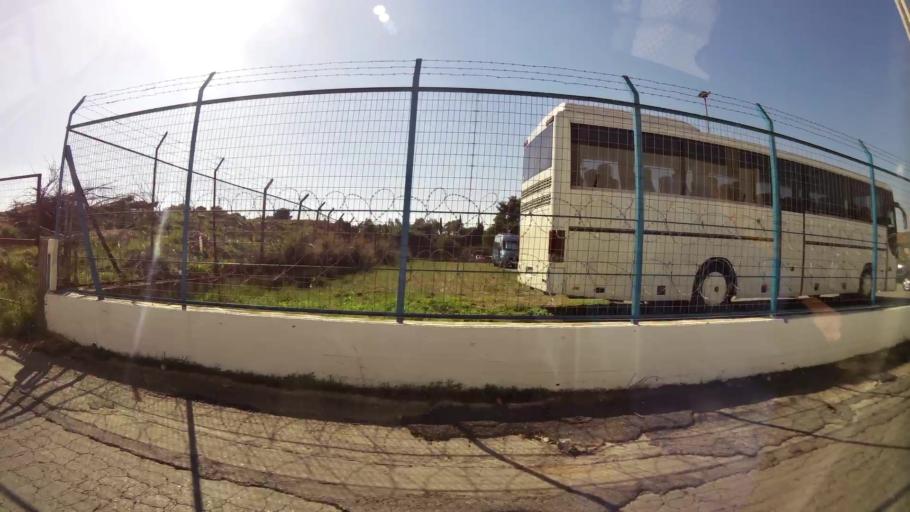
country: GR
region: Attica
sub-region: Nomarchia Athinas
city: Lykovrysi
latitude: 38.0874
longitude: 23.7806
